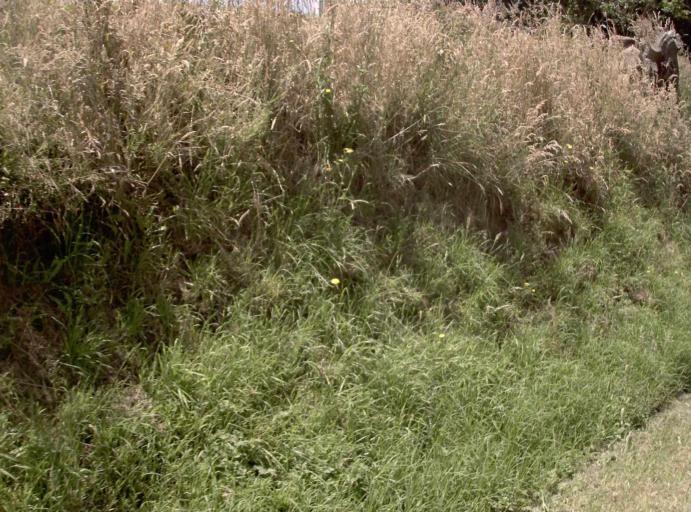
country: AU
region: Victoria
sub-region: Bass Coast
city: North Wonthaggi
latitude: -38.7107
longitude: 146.0898
